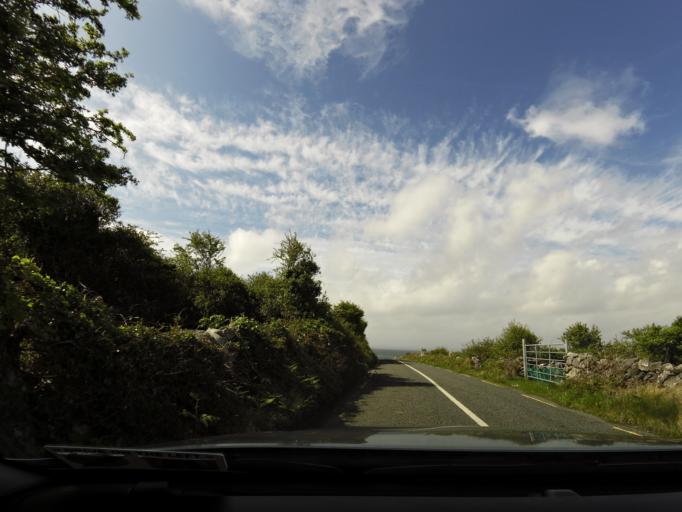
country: IE
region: Connaught
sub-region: County Galway
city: Bearna
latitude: 53.1464
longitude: -9.2367
